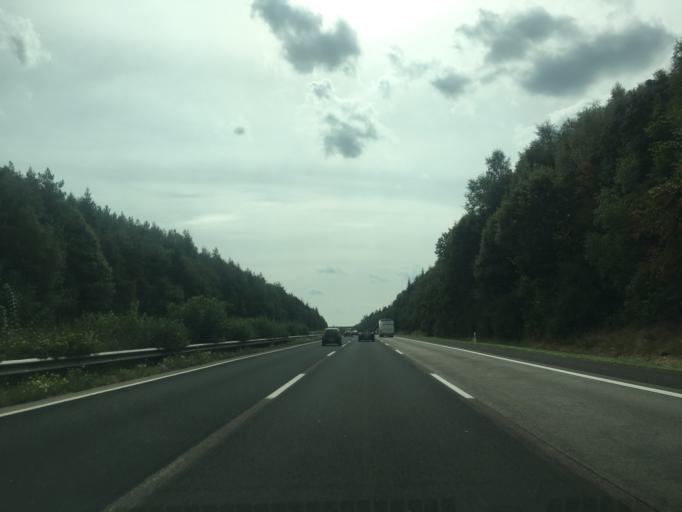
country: DE
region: Rheinland-Pfalz
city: Birkheim
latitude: 50.1049
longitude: 7.6037
